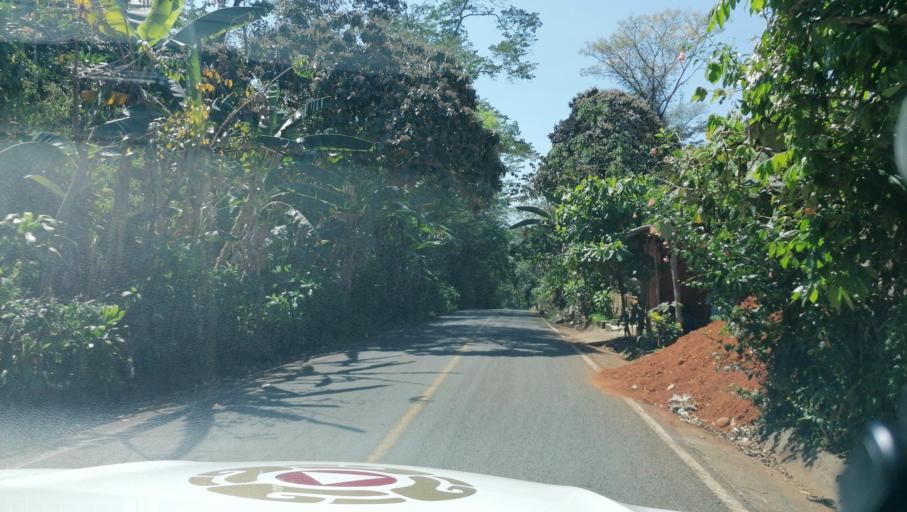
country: MX
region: Chiapas
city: Veinte de Noviembre
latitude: 15.0063
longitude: -92.2292
